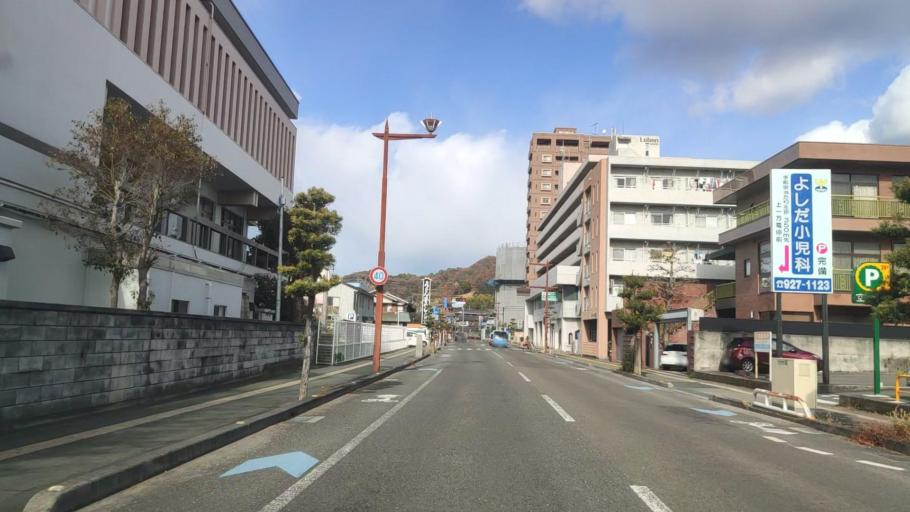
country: JP
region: Ehime
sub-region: Shikoku-chuo Shi
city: Matsuyama
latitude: 33.8508
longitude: 132.7809
